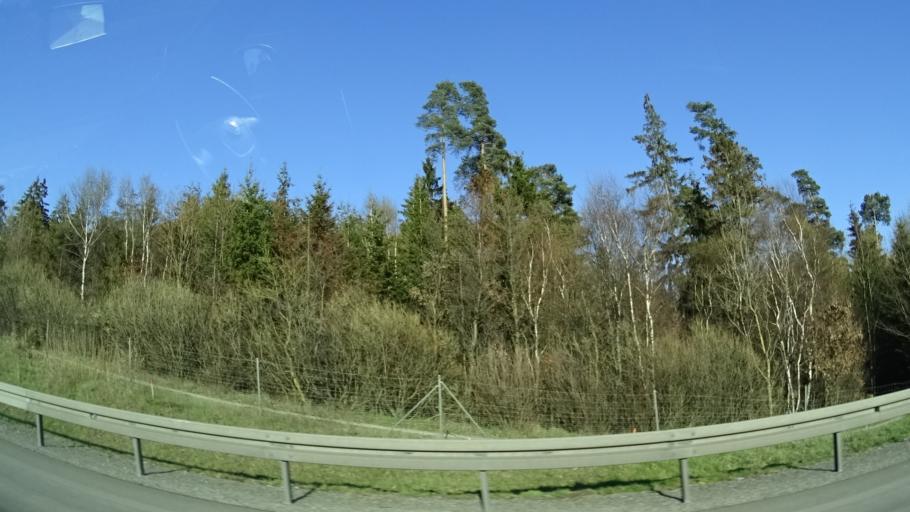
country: DE
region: Bavaria
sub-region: Upper Franconia
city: Gefrees
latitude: 50.1354
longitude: 11.7423
